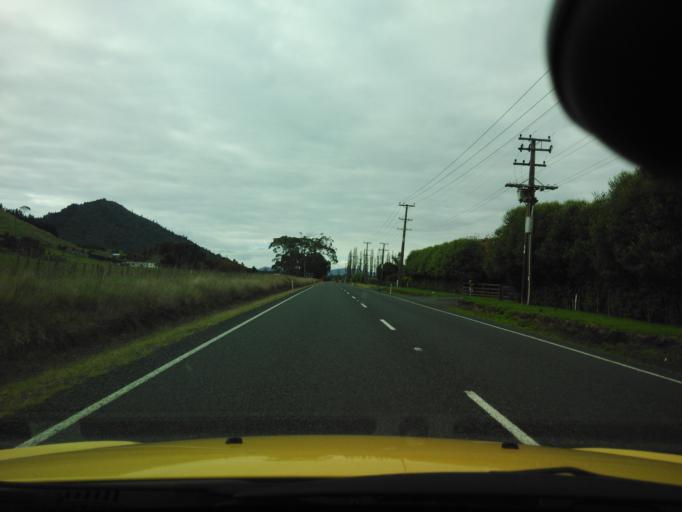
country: NZ
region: Waikato
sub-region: Waikato District
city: Ngaruawahia
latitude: -37.6232
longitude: 175.1739
